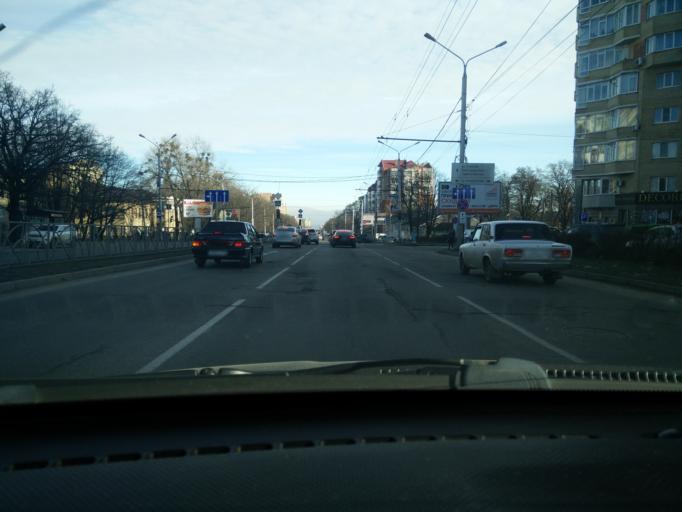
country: RU
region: Stavropol'skiy
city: Stavropol'
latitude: 45.0337
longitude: 41.9573
